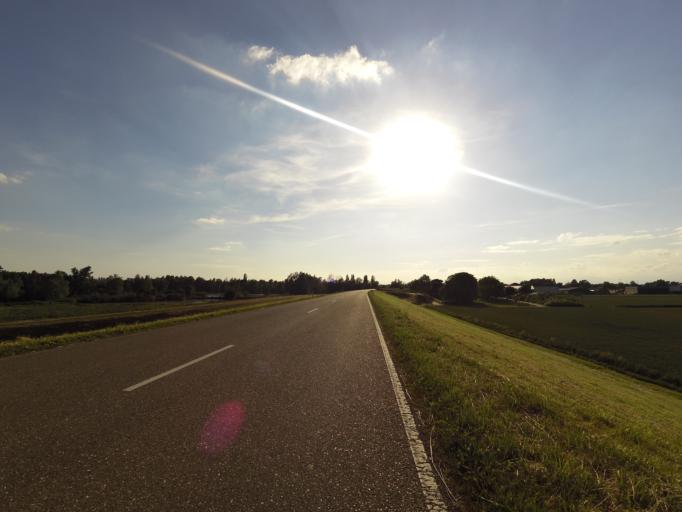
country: NL
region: Gelderland
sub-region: Gemeente Zevenaar
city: Zevenaar
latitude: 51.8853
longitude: 6.0542
